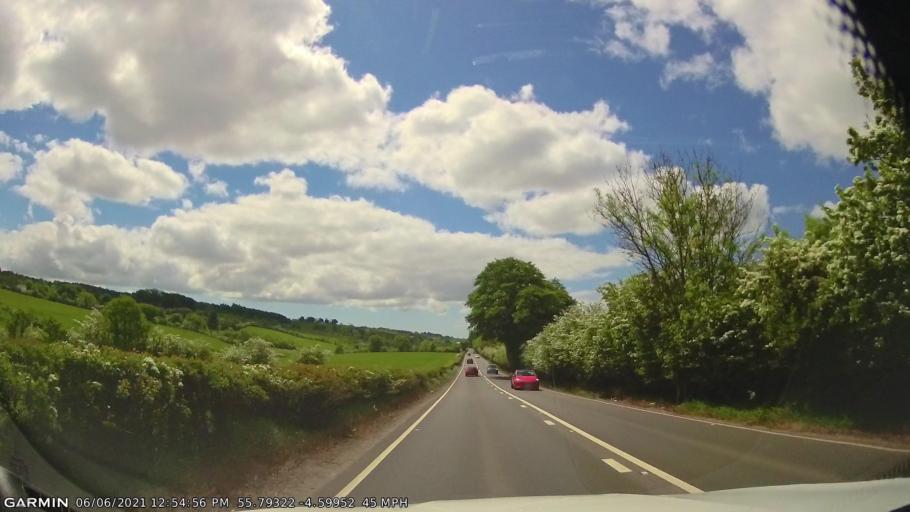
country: GB
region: Scotland
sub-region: Renfrewshire
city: Lochwinnoch
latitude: 55.7932
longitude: -4.5994
